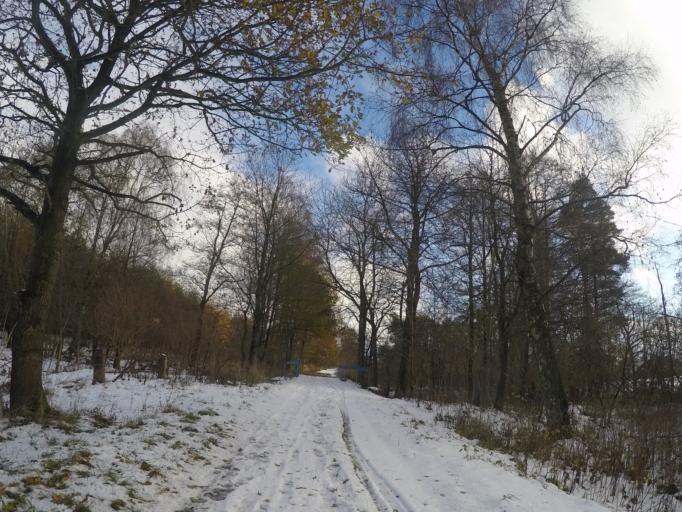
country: SE
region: Skane
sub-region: Lunds Kommun
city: Lund
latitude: 55.7850
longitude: 13.2239
